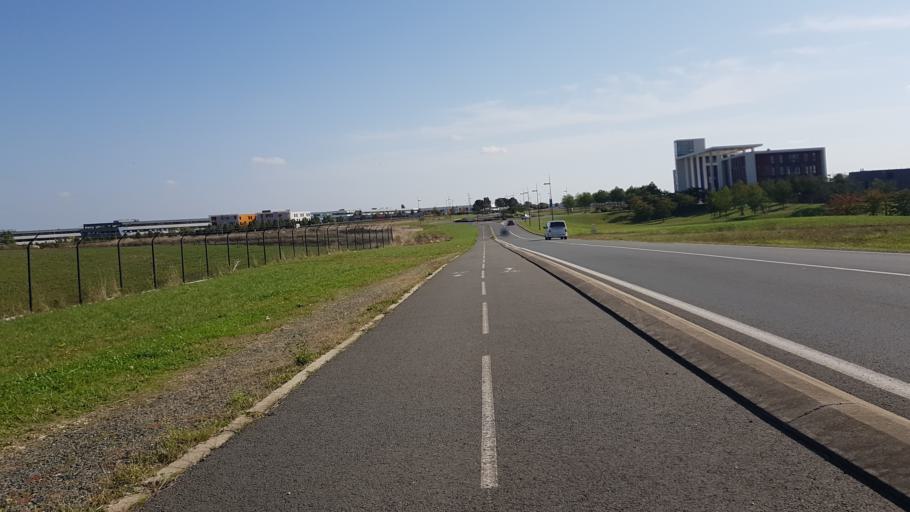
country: FR
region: Poitou-Charentes
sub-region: Departement de la Vienne
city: Chasseneuil-du-Poitou
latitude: 46.6565
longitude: 0.3575
